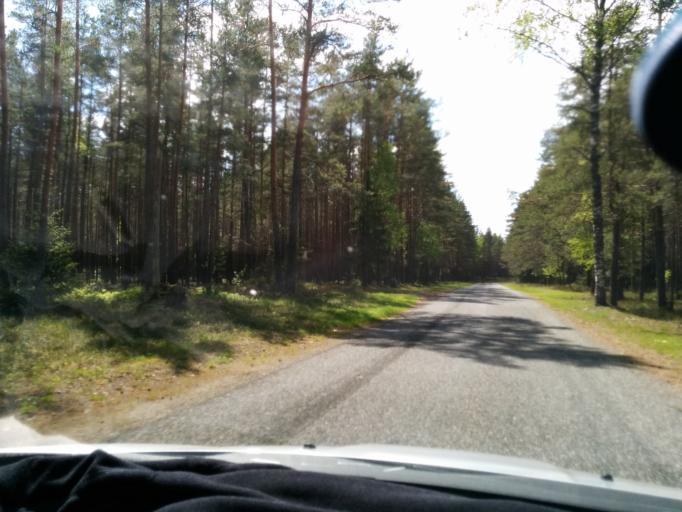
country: EE
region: Harju
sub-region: Loksa linn
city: Loksa
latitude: 59.5480
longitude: 25.9417
